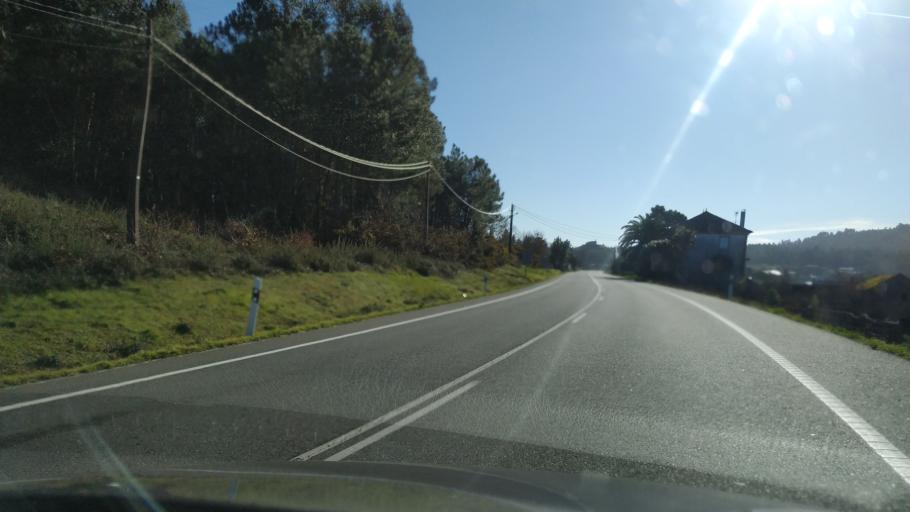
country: ES
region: Galicia
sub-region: Provincia da Coruna
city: Ribeira
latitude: 42.7524
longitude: -8.3528
